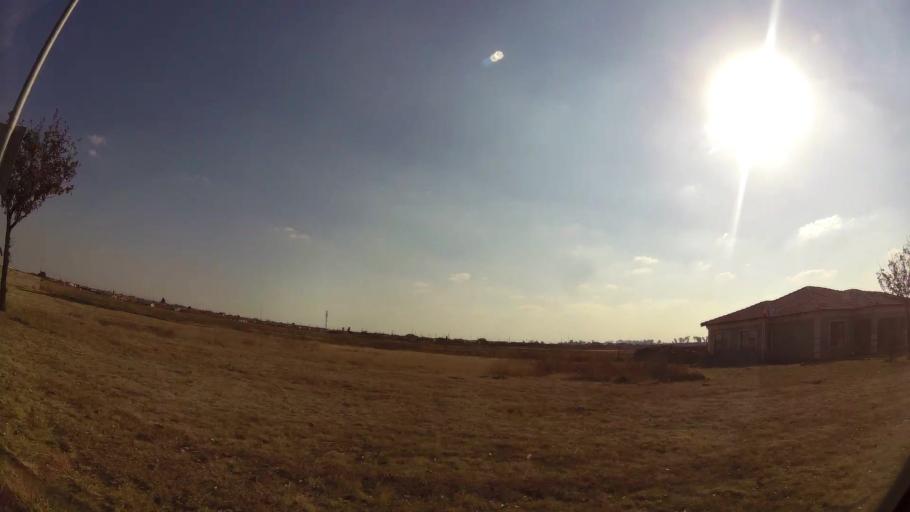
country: ZA
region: Gauteng
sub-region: Ekurhuleni Metropolitan Municipality
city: Brakpan
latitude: -26.2266
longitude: 28.3325
